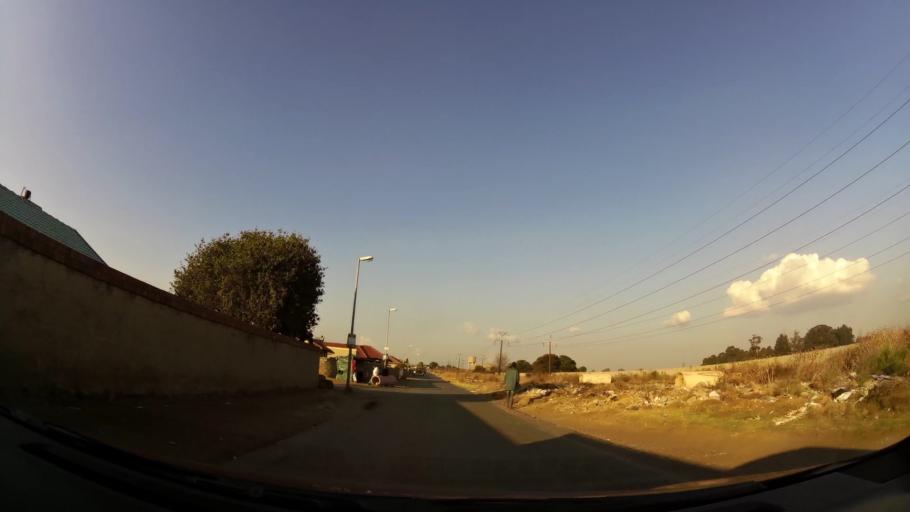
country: ZA
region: Gauteng
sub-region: City of Johannesburg Metropolitan Municipality
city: Soweto
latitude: -26.2325
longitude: 27.8449
